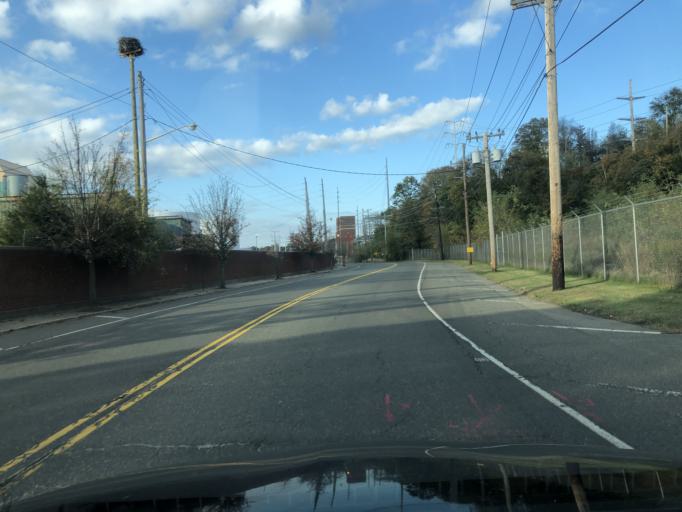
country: US
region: New York
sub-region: Nassau County
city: Glenwood Landing
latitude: 40.8254
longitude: -73.6470
